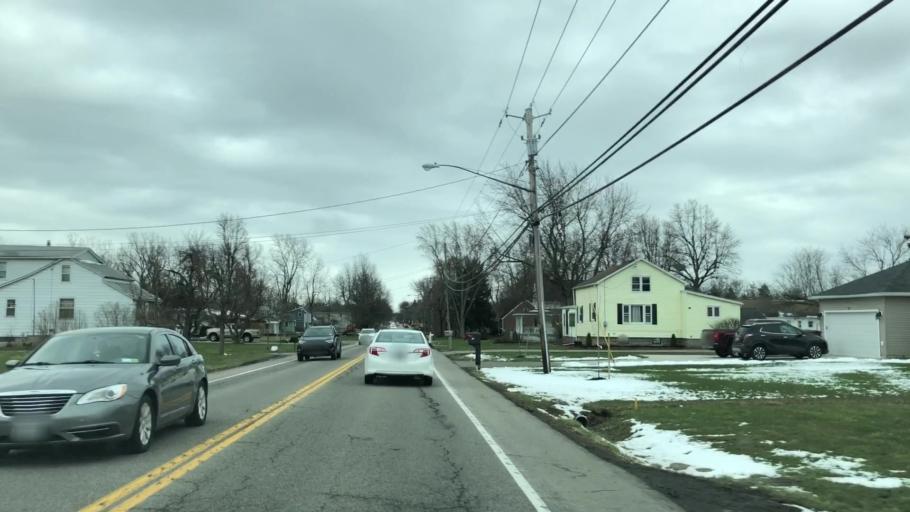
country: US
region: New York
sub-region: Erie County
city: Lancaster
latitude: 42.8846
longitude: -78.6768
